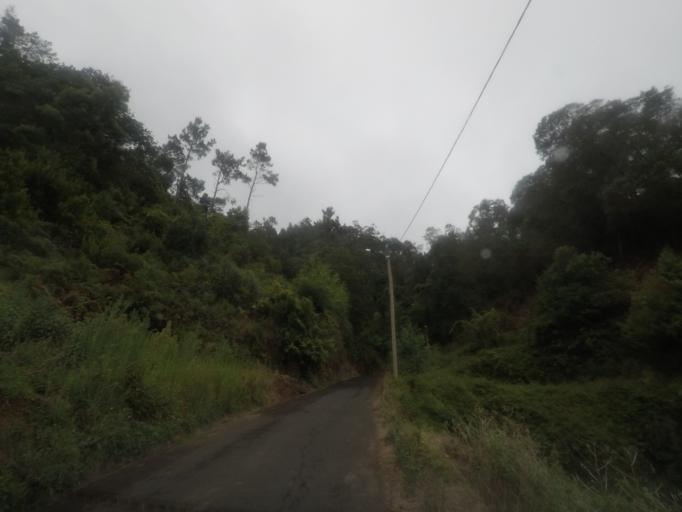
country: PT
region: Madeira
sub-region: Santana
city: Santana
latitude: 32.7668
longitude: -16.8509
